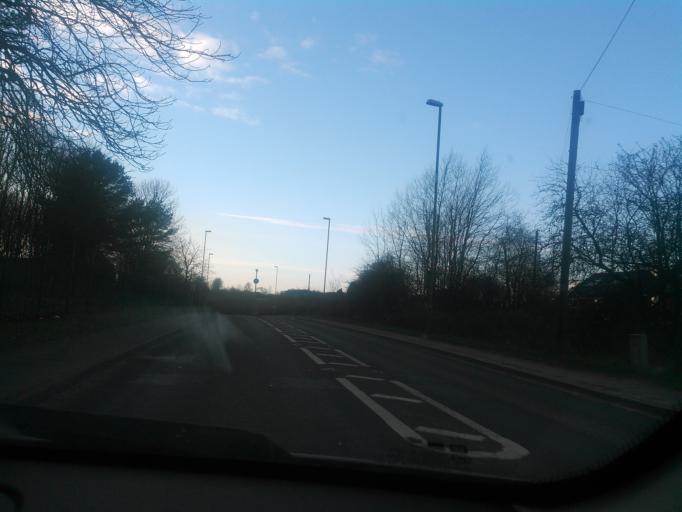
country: GB
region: England
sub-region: Shropshire
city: Stoke upon Tern
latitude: 52.8814
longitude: -2.5334
